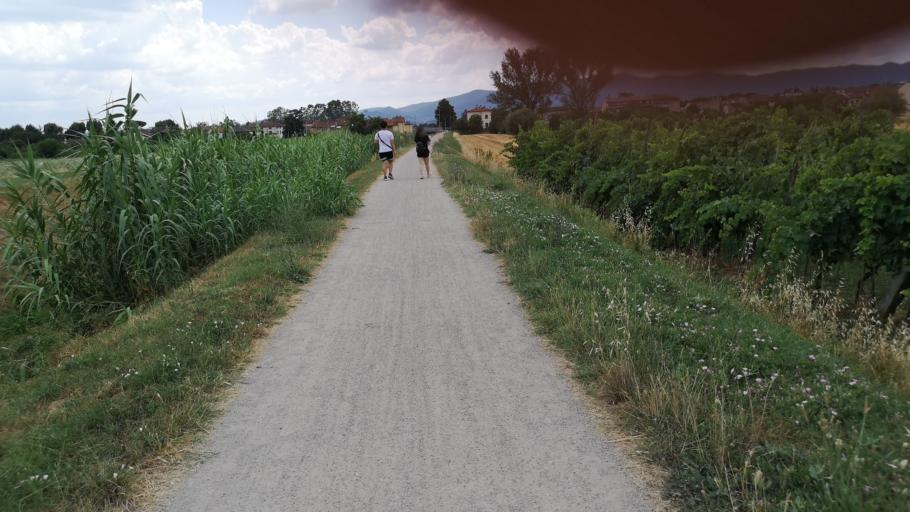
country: IT
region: Tuscany
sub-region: Provincia di Prato
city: Prato
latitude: 43.8775
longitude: 11.0462
